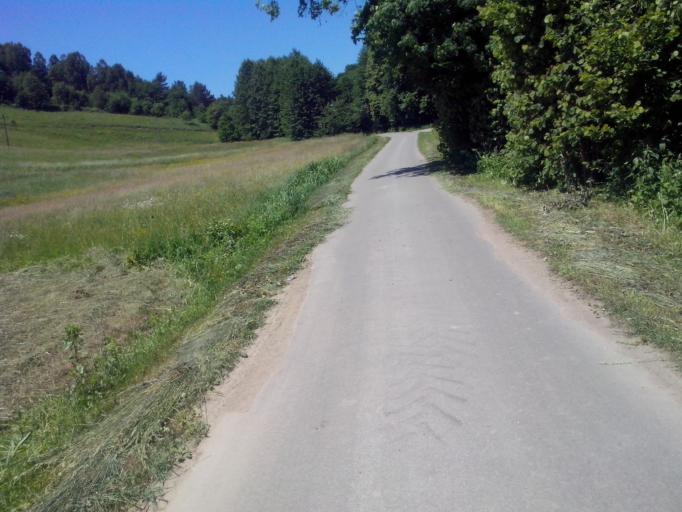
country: PL
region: Subcarpathian Voivodeship
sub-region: Powiat krosnienski
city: Leki
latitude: 49.8204
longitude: 21.6742
